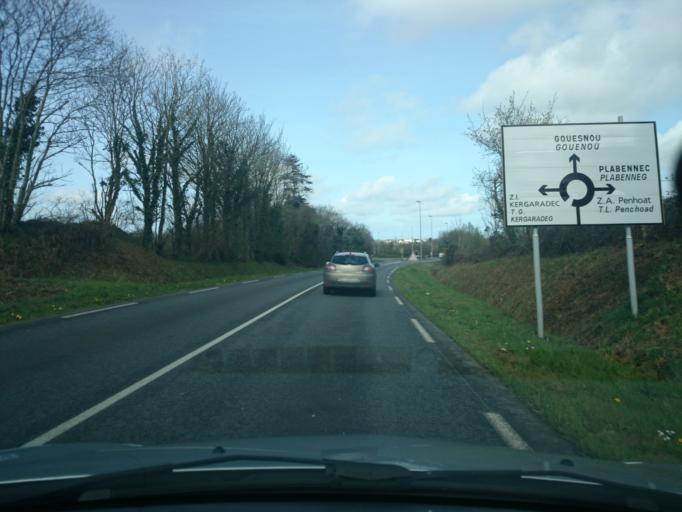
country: FR
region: Brittany
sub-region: Departement du Finistere
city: Gouesnou
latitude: 48.4424
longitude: -4.4542
